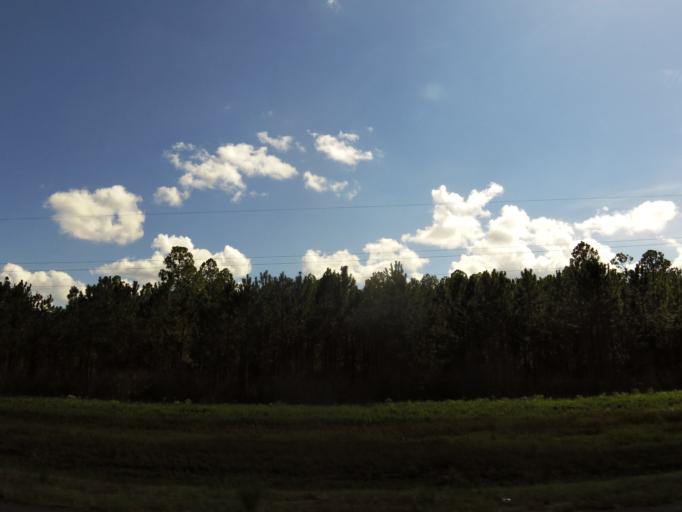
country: US
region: Florida
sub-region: Hamilton County
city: Jasper
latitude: 30.6790
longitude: -82.6082
